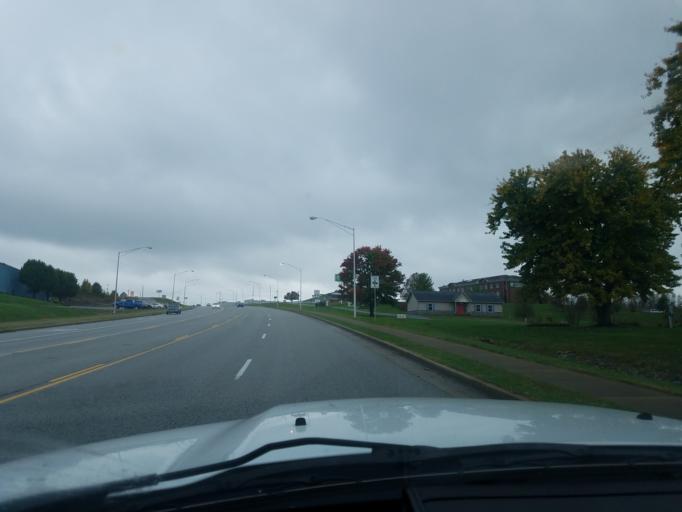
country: US
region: Kentucky
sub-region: Taylor County
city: Campbellsville
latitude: 37.3500
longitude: -85.3750
